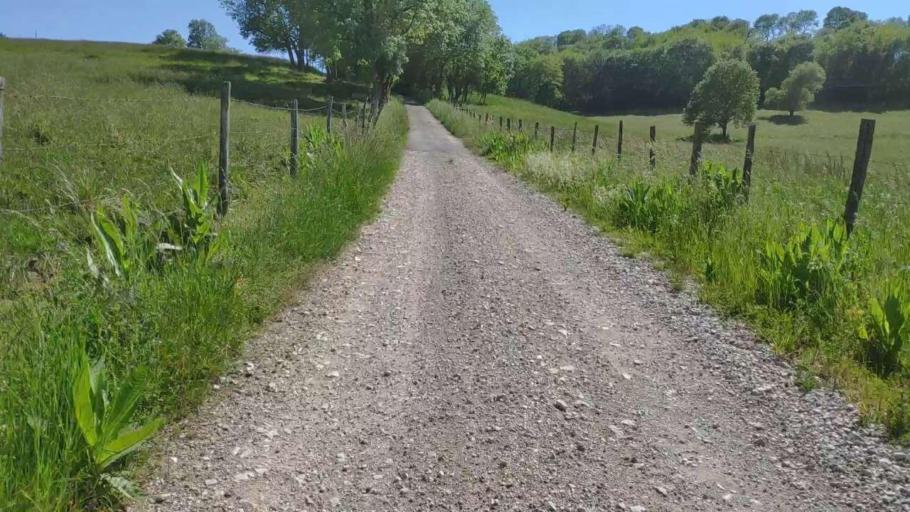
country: FR
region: Franche-Comte
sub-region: Departement du Jura
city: Perrigny
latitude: 46.7264
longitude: 5.5848
